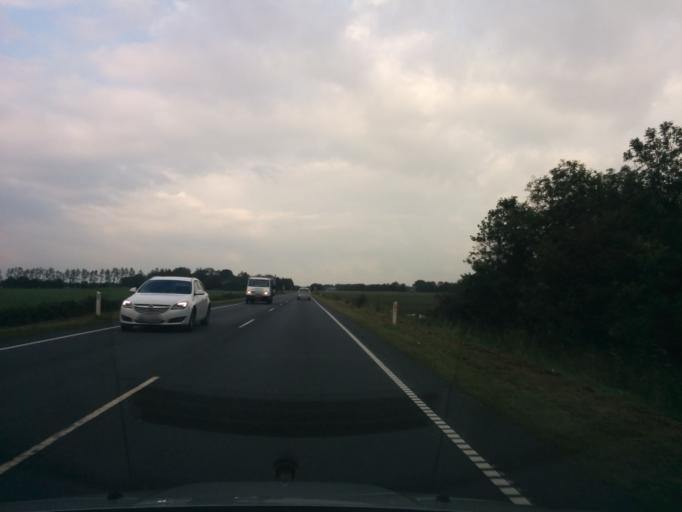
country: DK
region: South Denmark
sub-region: Esbjerg Kommune
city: Bramming
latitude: 55.6119
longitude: 8.7462
